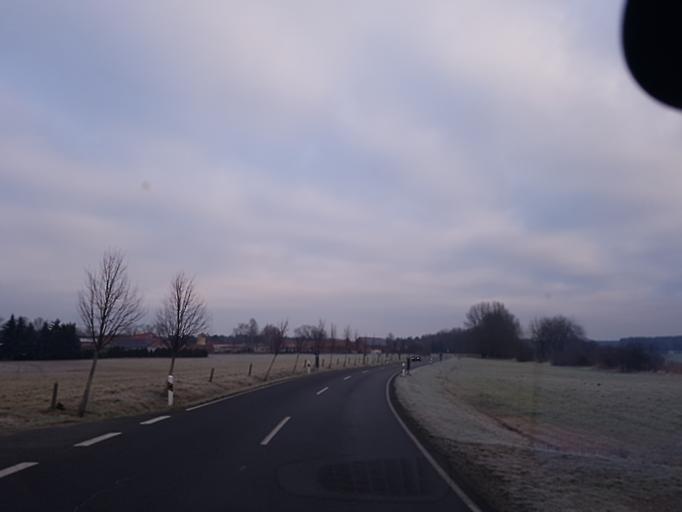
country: DE
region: Brandenburg
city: Finsterwalde
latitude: 51.6834
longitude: 13.7223
